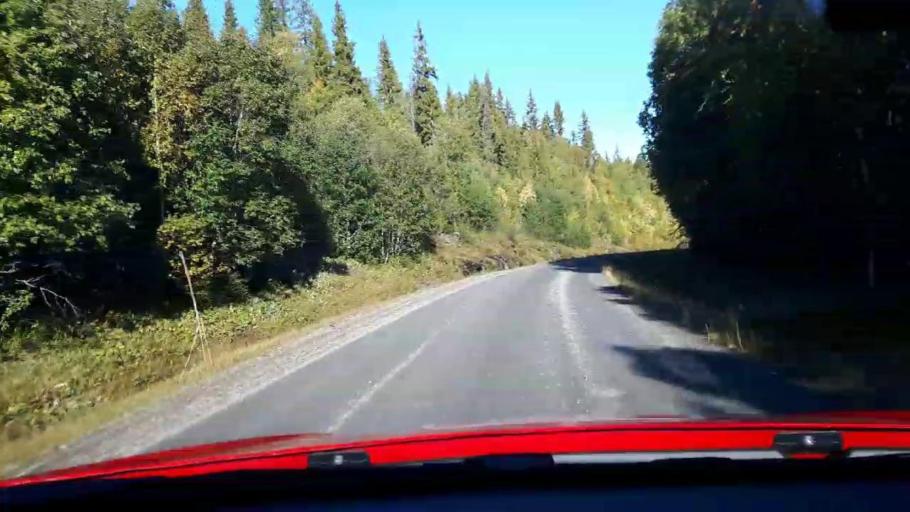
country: NO
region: Nord-Trondelag
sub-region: Lierne
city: Sandvika
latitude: 64.5692
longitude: 13.9044
